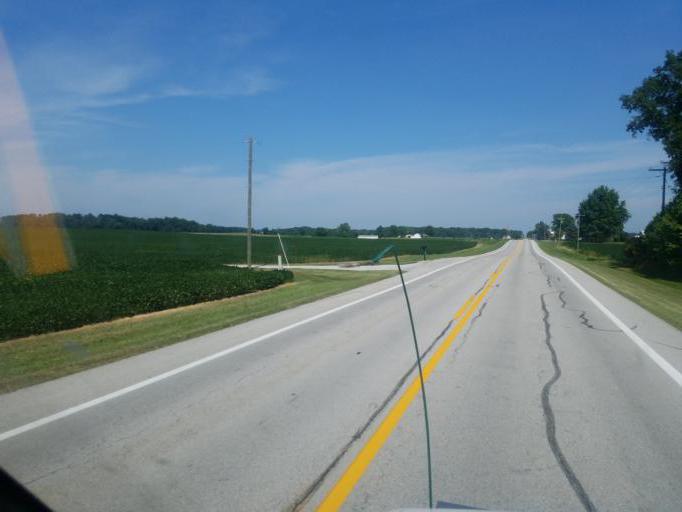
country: US
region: Ohio
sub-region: Shelby County
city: Botkins
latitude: 40.4968
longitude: -84.2007
